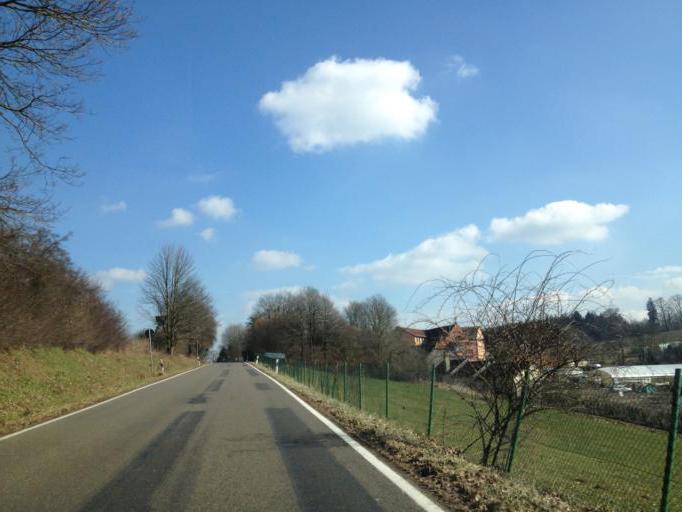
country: DE
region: Saarland
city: Sankt Wendel
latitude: 49.4690
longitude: 7.2009
